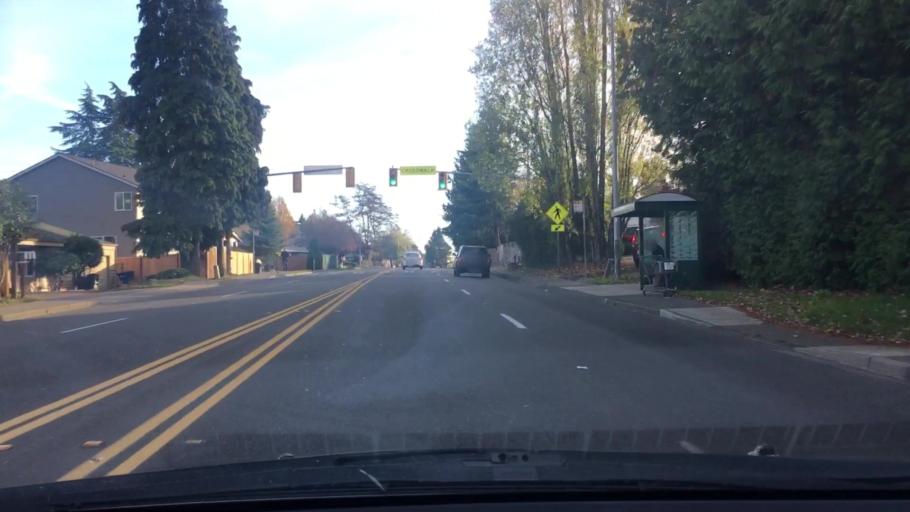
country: US
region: Washington
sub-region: King County
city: Burien
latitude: 47.4856
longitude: -122.3493
